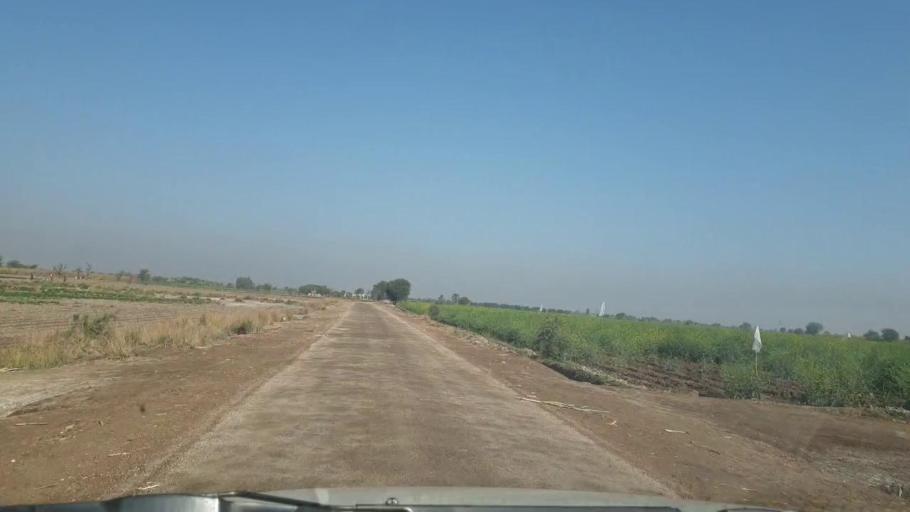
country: PK
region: Sindh
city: Mirpur Khas
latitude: 25.5052
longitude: 69.1479
